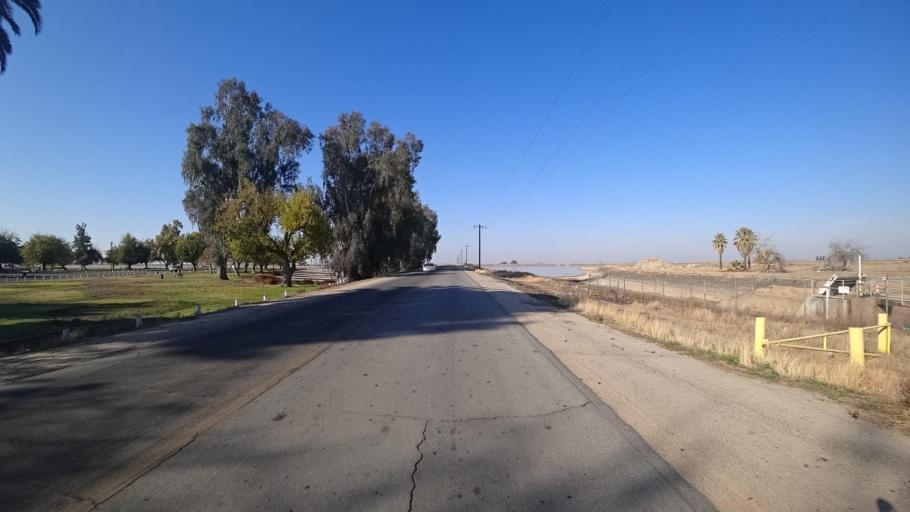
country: US
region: California
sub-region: Kern County
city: Delano
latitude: 35.7471
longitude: -119.1750
